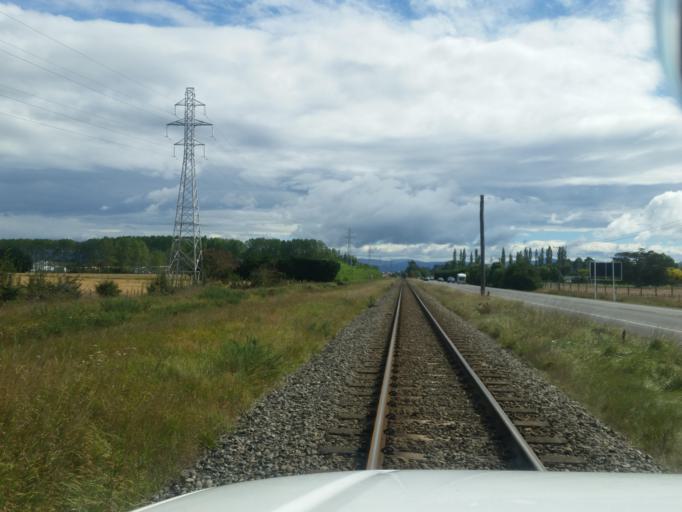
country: NZ
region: Canterbury
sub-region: Waimakariri District
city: Kaiapoi
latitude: -43.3372
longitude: 172.6097
